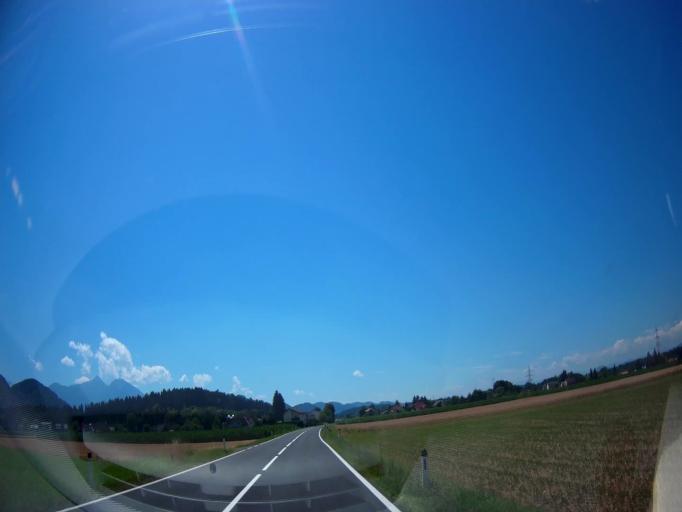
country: AT
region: Carinthia
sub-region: Politischer Bezirk Volkermarkt
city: Eberndorf
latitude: 46.6186
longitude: 14.6041
